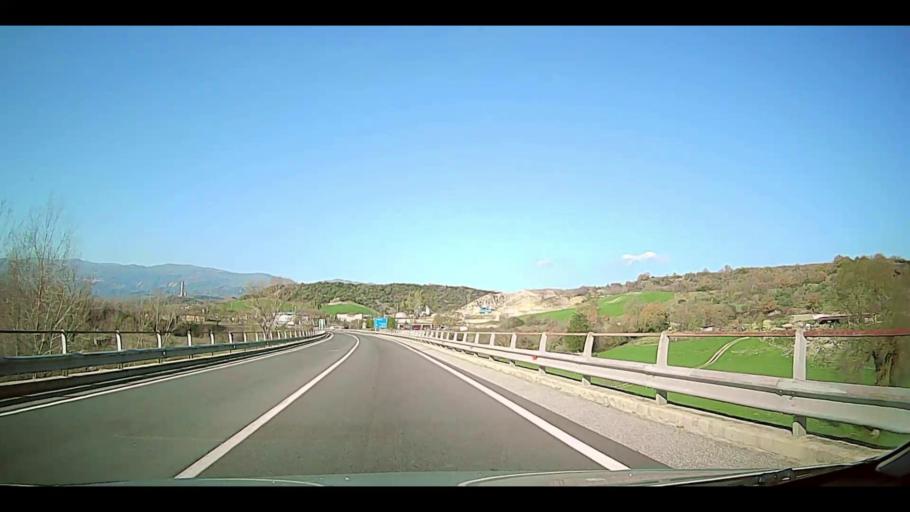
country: IT
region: Calabria
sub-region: Provincia di Crotone
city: Belvedere Spinello
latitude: 39.1885
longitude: 16.8511
